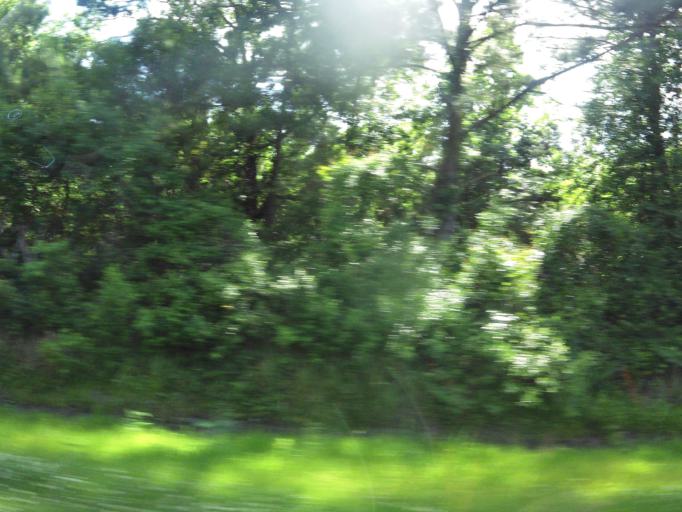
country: US
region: Florida
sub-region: Nassau County
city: Callahan
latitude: 30.5776
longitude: -81.8467
